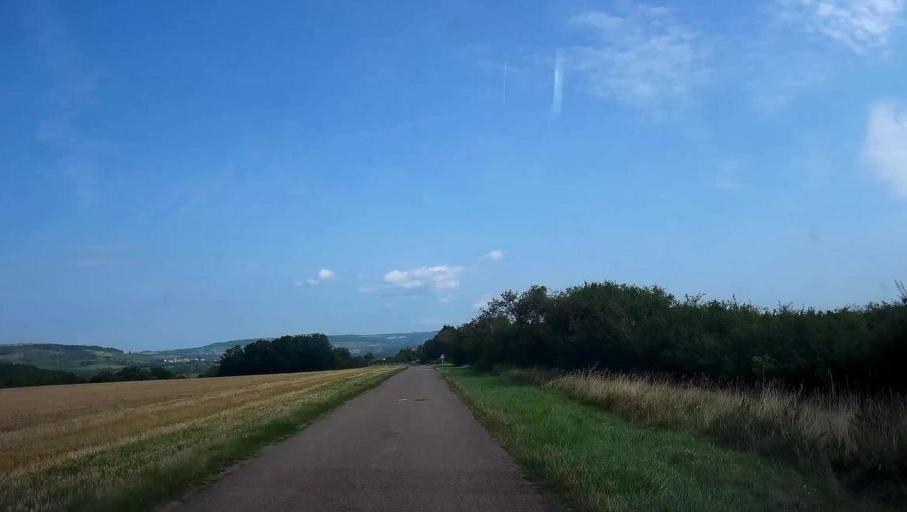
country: FR
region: Bourgogne
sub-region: Departement de la Cote-d'Or
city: Nolay
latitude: 46.9042
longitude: 4.6290
